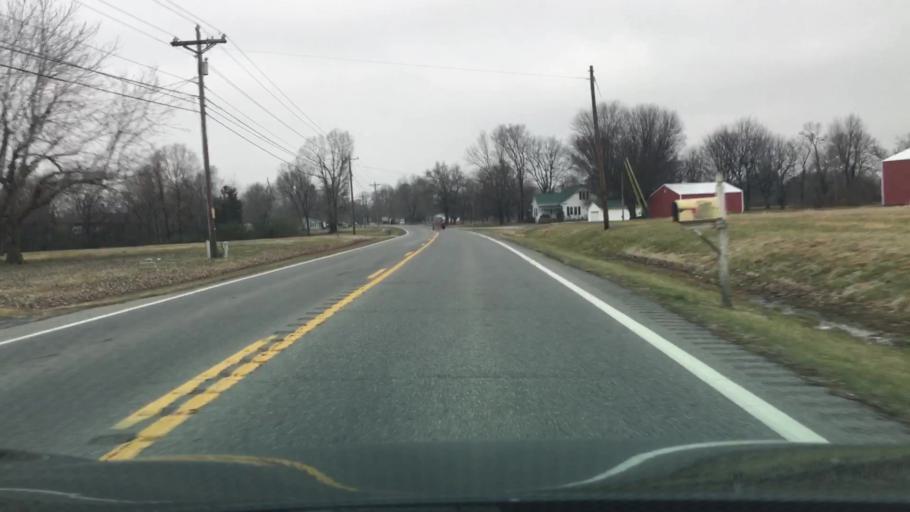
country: US
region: Kentucky
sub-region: Marshall County
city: Calvert City
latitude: 36.9679
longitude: -88.3854
